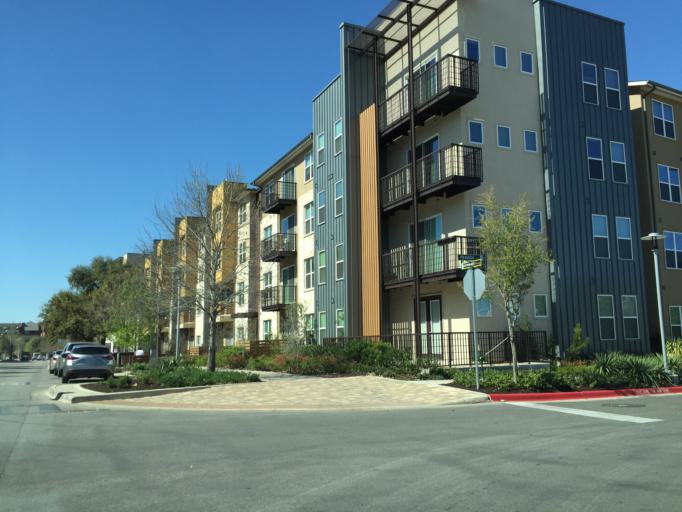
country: US
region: Texas
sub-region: Travis County
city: Wells Branch
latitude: 30.3992
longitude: -97.7218
